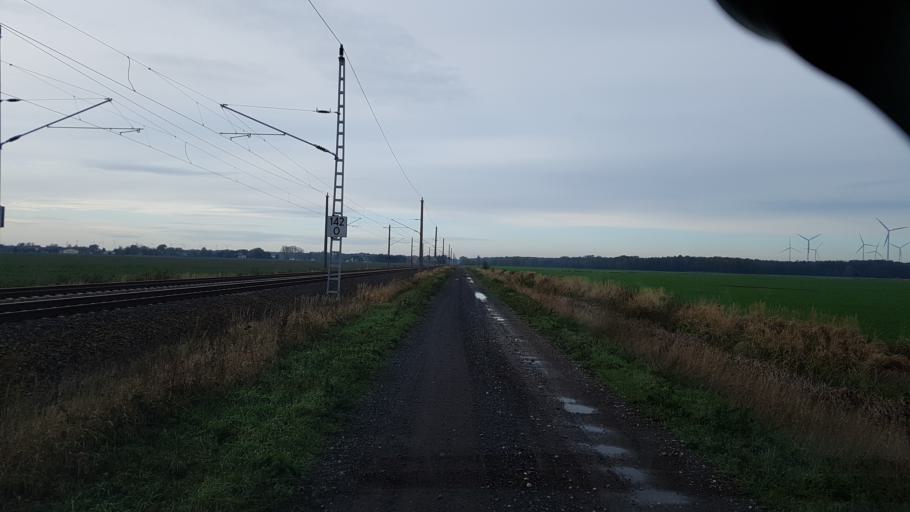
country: DE
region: Brandenburg
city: Falkenberg
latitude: 51.5501
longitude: 13.3106
